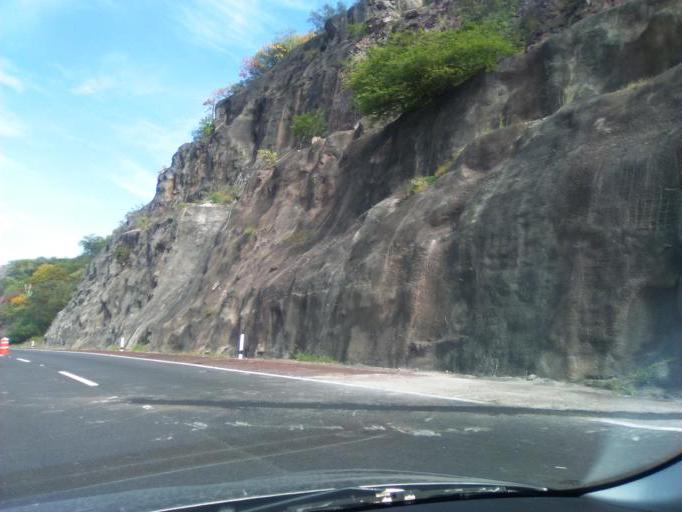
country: MX
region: Guerrero
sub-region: Huitzuco de los Figueroa
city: San Francisco Ozomatlan
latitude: 17.9514
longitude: -99.3568
